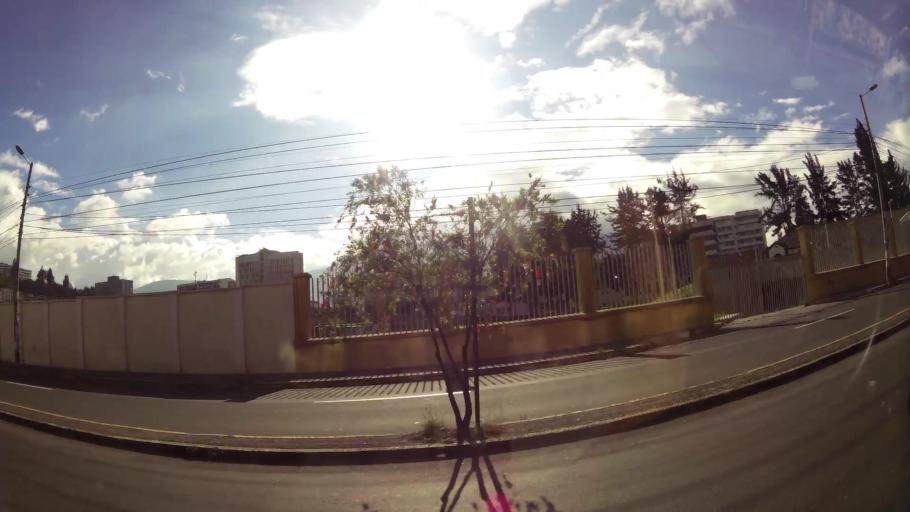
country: EC
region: Pichincha
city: Quito
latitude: -0.2116
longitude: -78.4882
